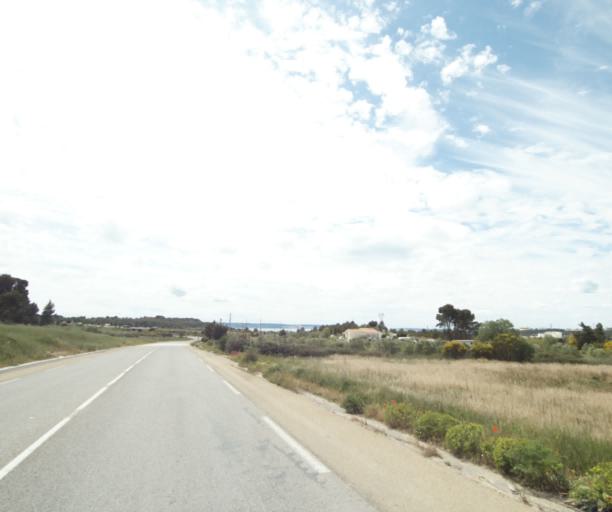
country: FR
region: Provence-Alpes-Cote d'Azur
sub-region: Departement des Bouches-du-Rhone
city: Rognac
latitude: 43.5095
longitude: 5.2402
